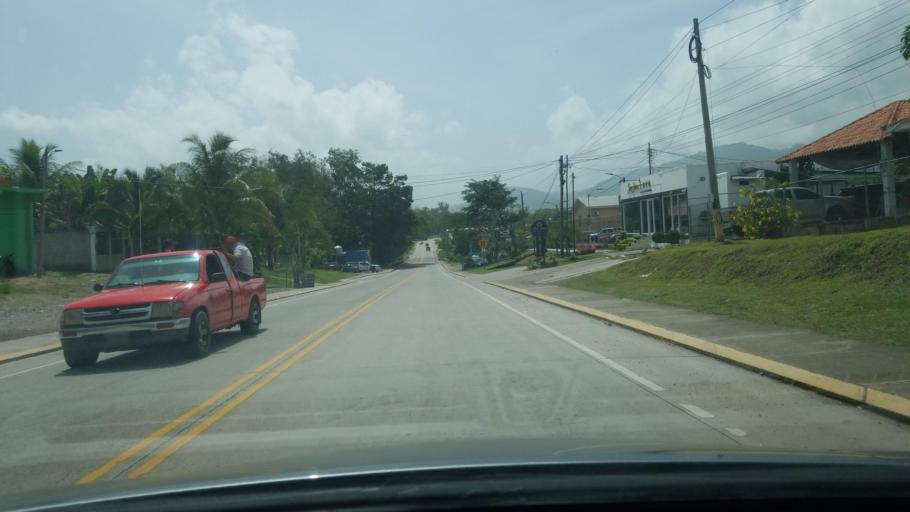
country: HN
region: Copan
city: La Entrada
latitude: 15.0695
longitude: -88.7702
